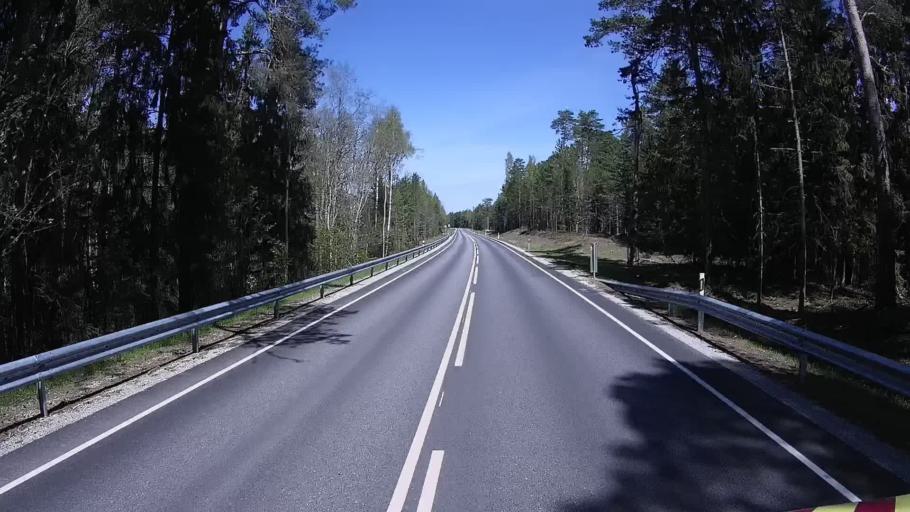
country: EE
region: Harju
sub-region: Nissi vald
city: Turba
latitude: 59.1323
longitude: 24.0730
